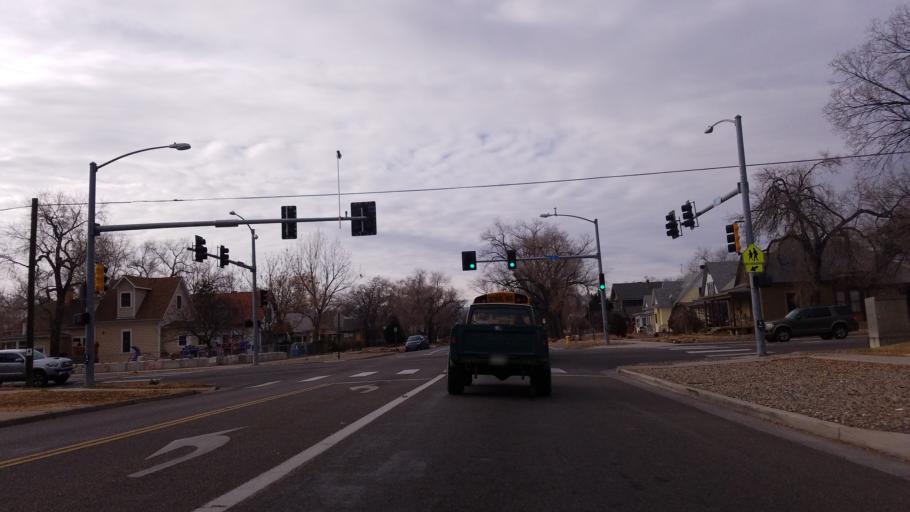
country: US
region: Colorado
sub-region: Mesa County
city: Grand Junction
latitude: 39.0704
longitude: -108.5520
